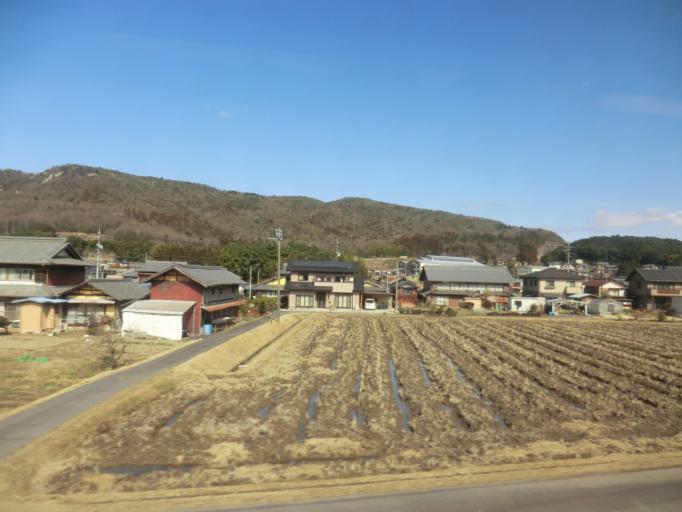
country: JP
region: Gifu
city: Mizunami
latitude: 35.3991
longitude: 137.2894
